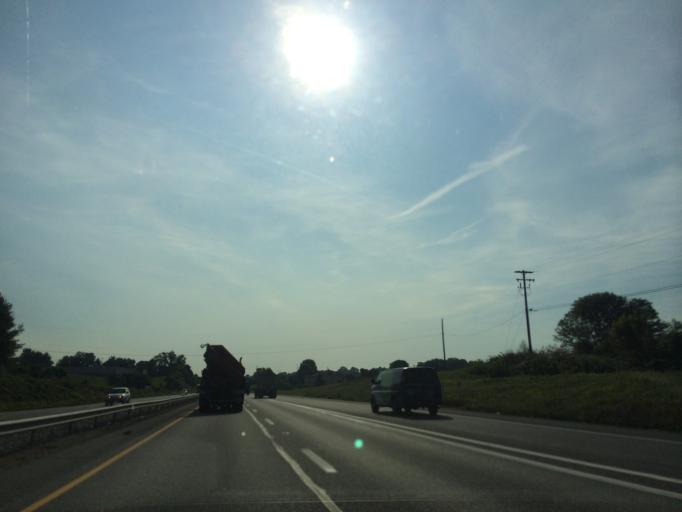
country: US
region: Pennsylvania
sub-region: Lancaster County
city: Mountville
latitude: 40.0393
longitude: -76.4524
